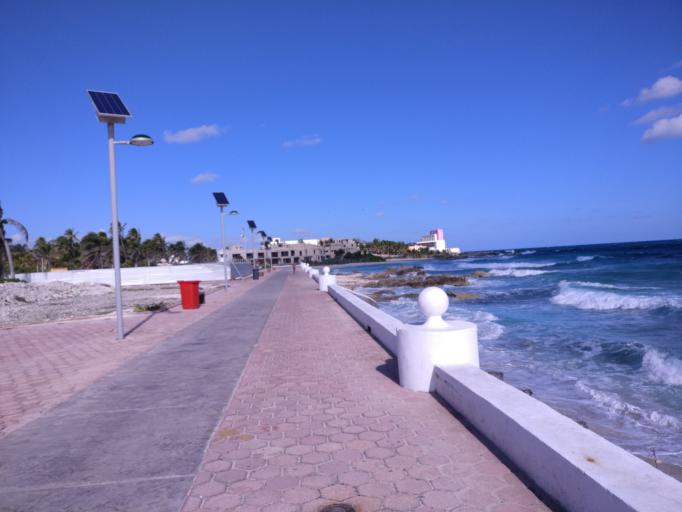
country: MX
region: Quintana Roo
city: Isla Mujeres
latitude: 21.2581
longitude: -86.7460
